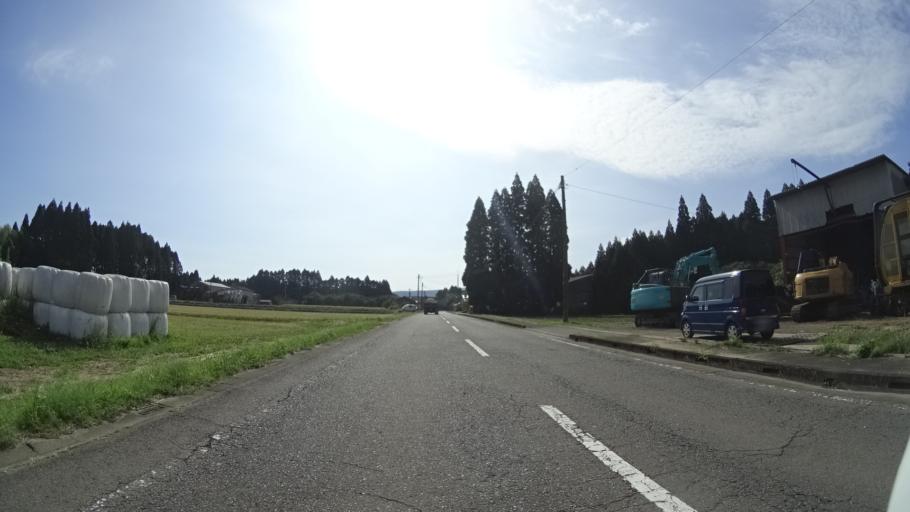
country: JP
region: Miyazaki
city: Kobayashi
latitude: 32.0256
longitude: 130.8301
